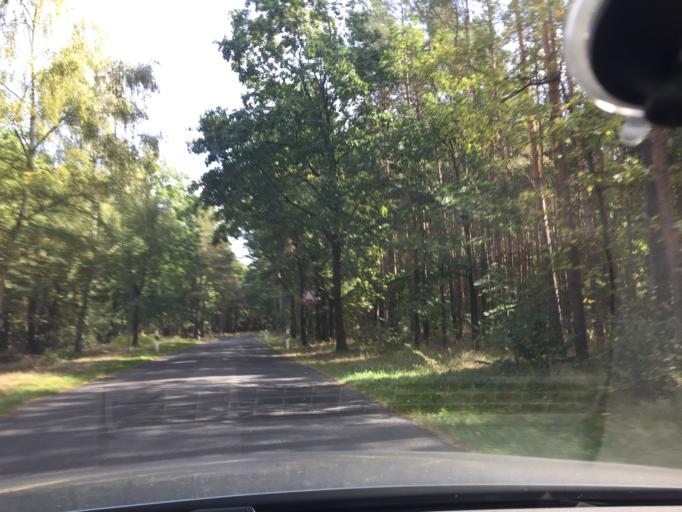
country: DE
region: Brandenburg
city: Grunheide
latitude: 52.3699
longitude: 13.8140
